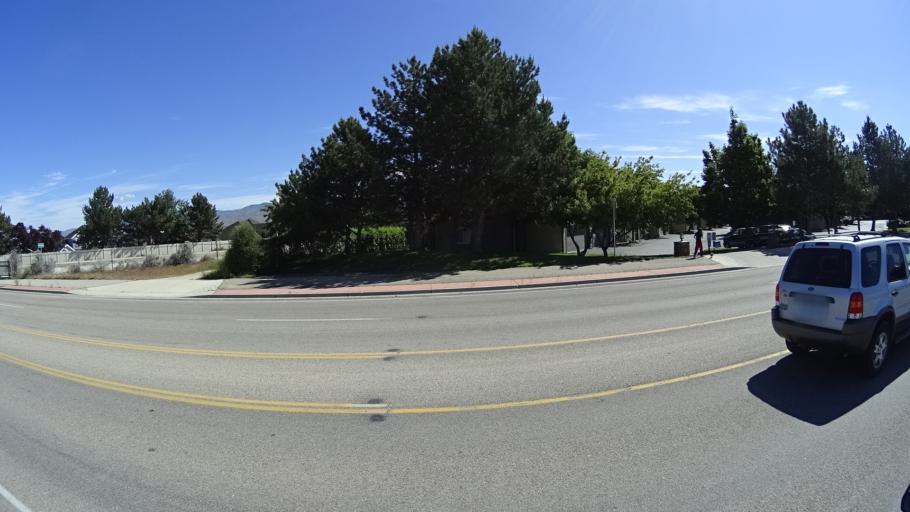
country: US
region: Idaho
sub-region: Ada County
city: Boise
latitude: 43.5663
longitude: -116.1796
